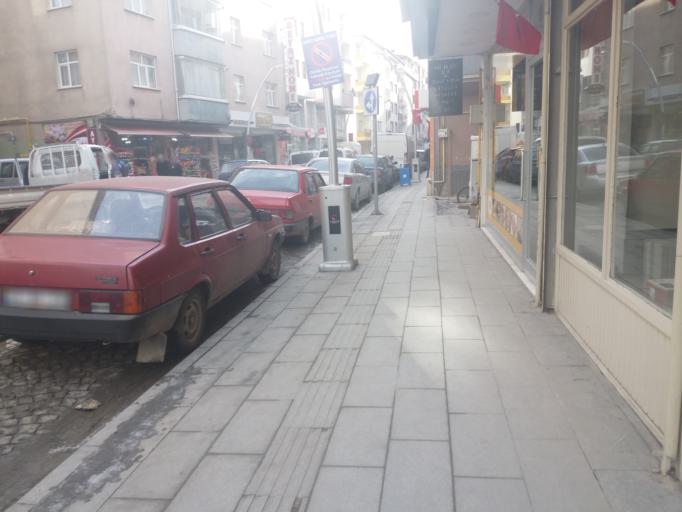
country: TR
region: Gumushane
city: Gumushkhane
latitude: 40.4611
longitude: 39.4736
